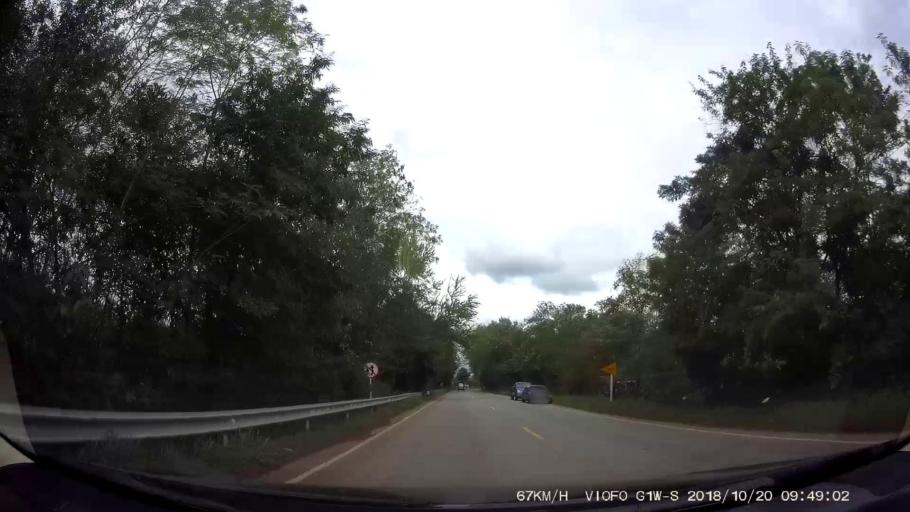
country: TH
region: Chaiyaphum
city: Khon San
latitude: 16.5158
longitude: 101.9076
